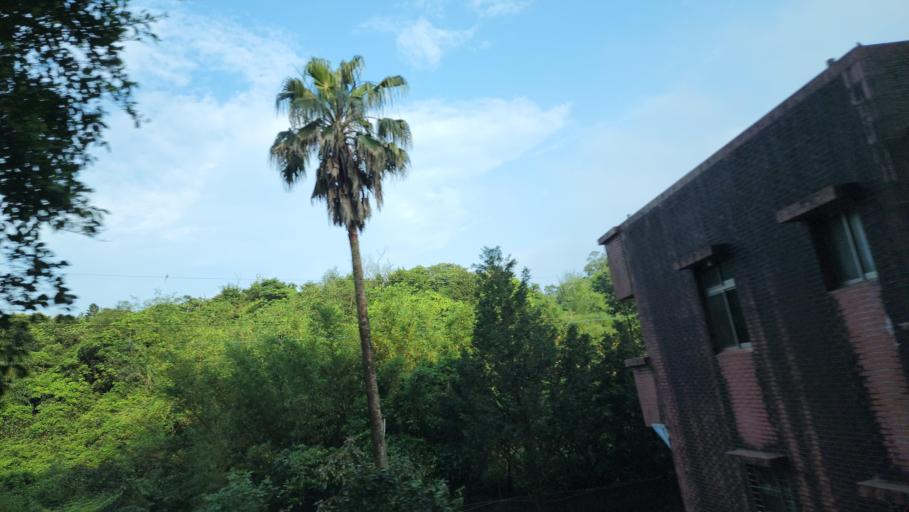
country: TW
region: Taiwan
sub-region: Keelung
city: Keelung
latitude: 25.1777
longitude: 121.6499
